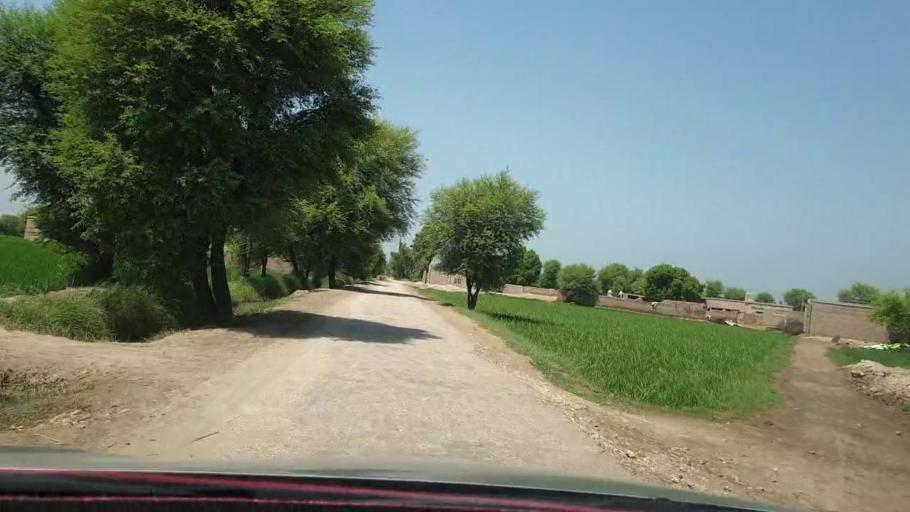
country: PK
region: Sindh
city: Warah
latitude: 27.5224
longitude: 67.8148
